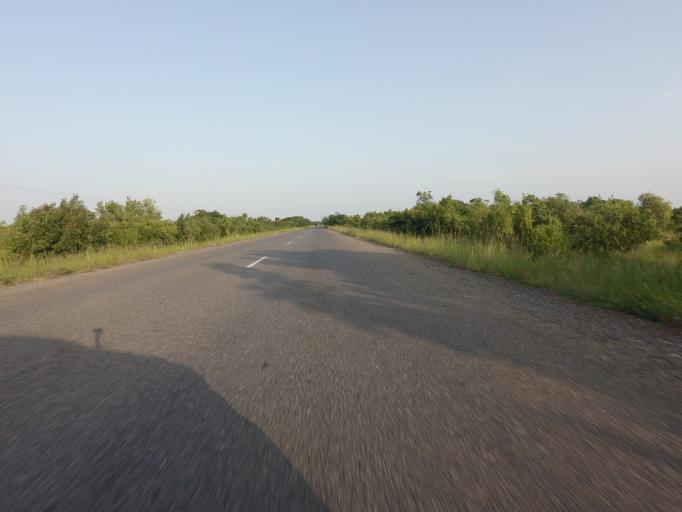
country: GH
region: Volta
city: Anloga
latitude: 5.9567
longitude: 0.6690
